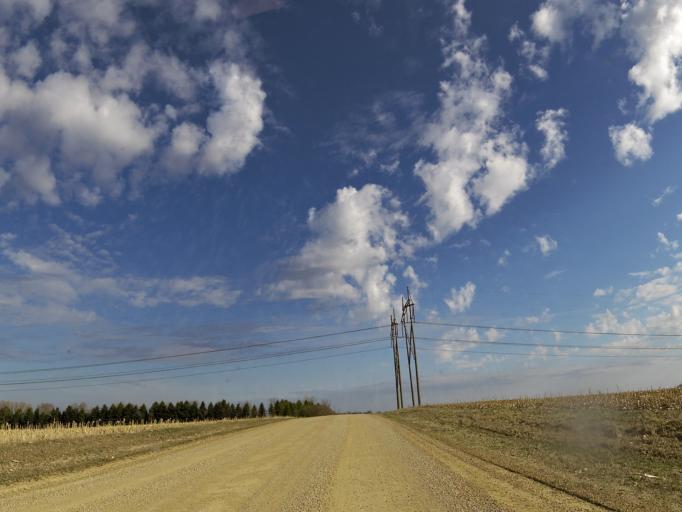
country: US
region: Minnesota
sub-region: Dakota County
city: Hastings
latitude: 44.8139
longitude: -92.8417
